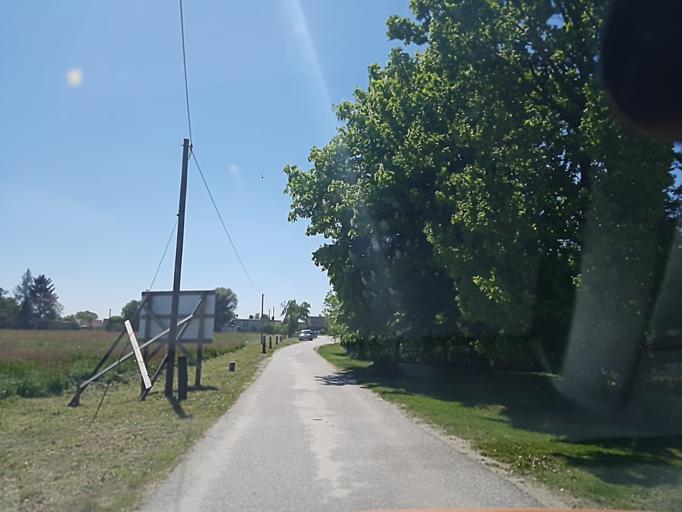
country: DE
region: Brandenburg
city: Sallgast
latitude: 51.6208
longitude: 13.8089
